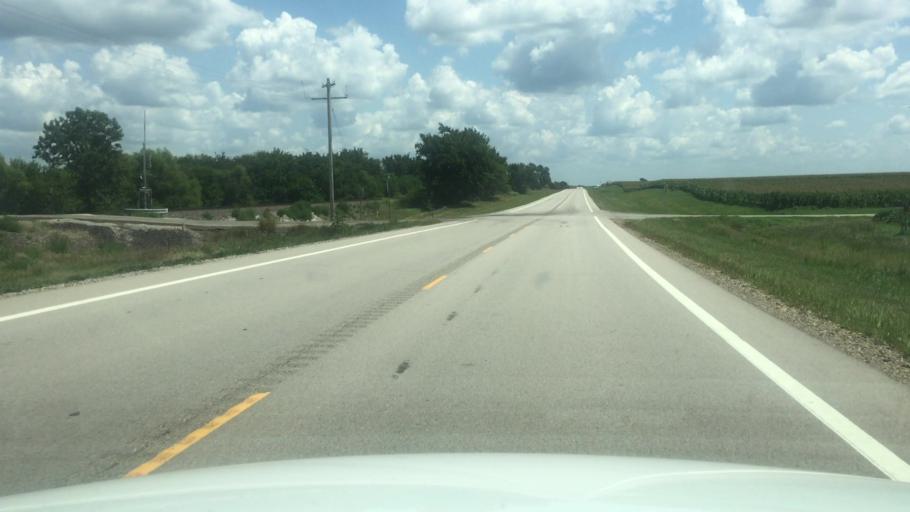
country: US
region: Kansas
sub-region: Brown County
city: Horton
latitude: 39.6586
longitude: -95.3781
